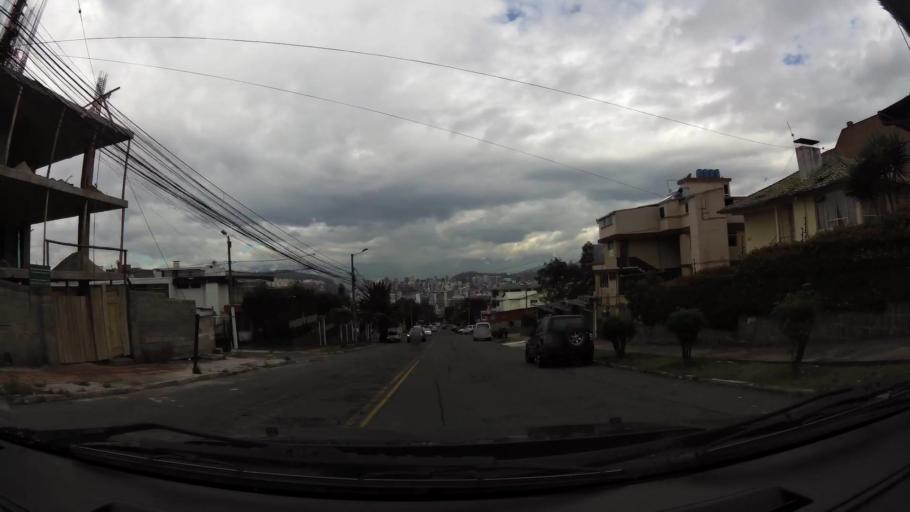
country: EC
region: Pichincha
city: Quito
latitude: -0.1869
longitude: -78.5006
